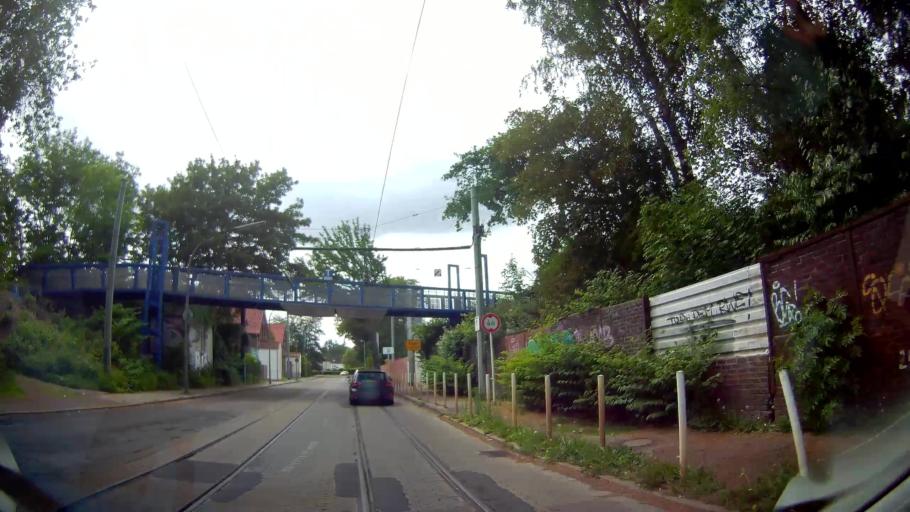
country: DE
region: North Rhine-Westphalia
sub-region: Regierungsbezirk Dusseldorf
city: Essen
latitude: 51.5035
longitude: 7.0562
